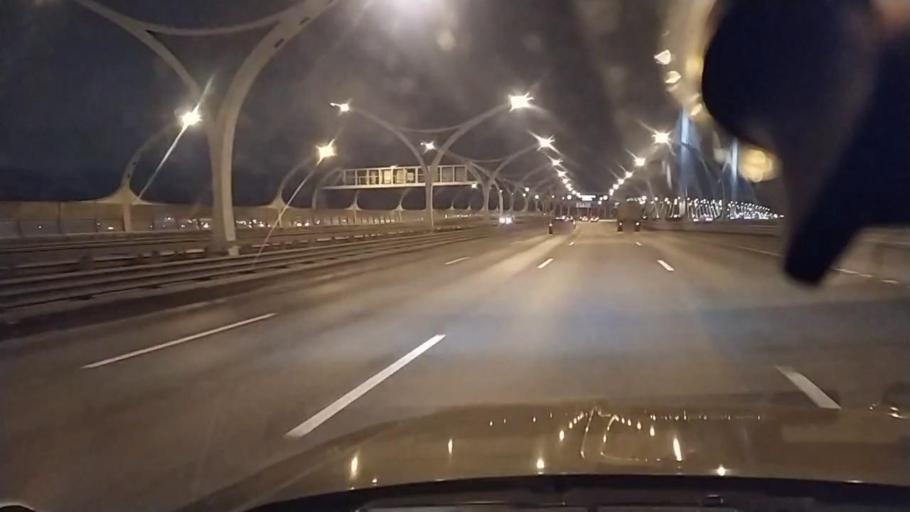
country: RU
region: St.-Petersburg
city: Staraya Derevnya
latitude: 59.9722
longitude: 30.2135
